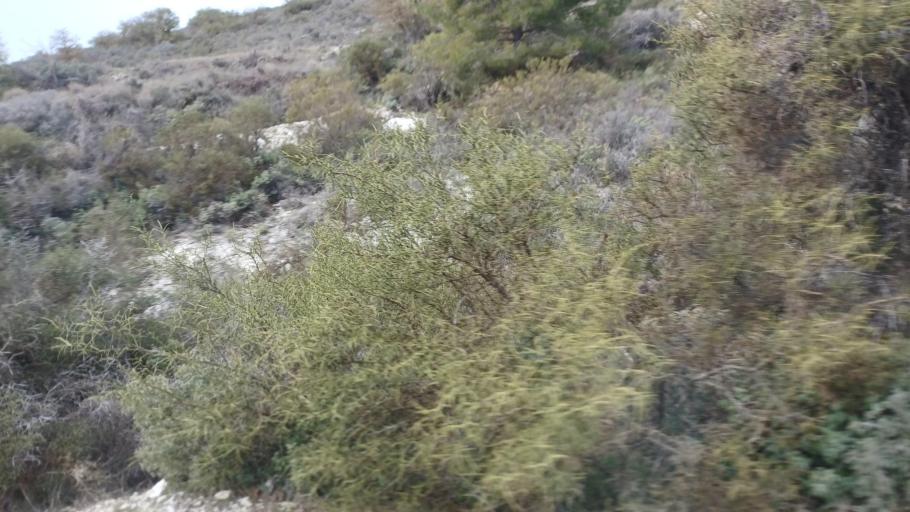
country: CY
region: Limassol
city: Pachna
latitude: 34.8663
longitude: 32.8031
